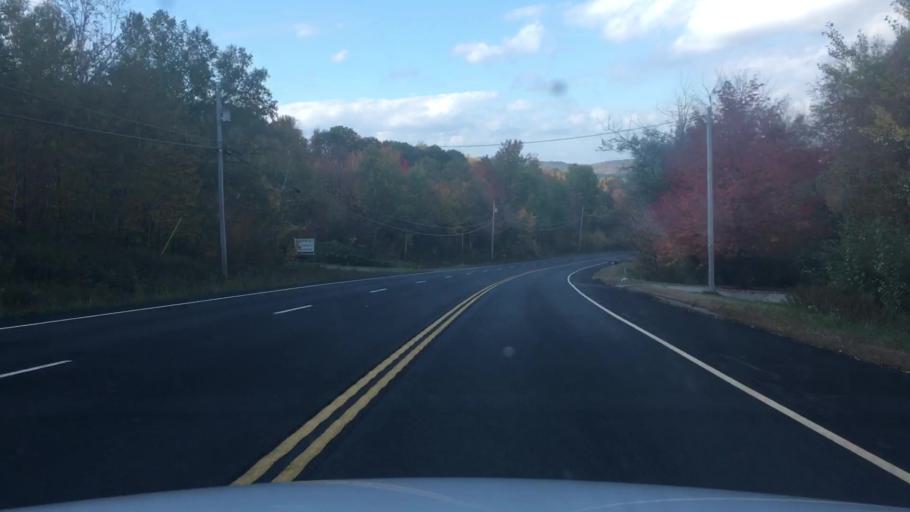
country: US
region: Maine
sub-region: Waldo County
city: Palermo
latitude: 44.3715
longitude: -69.3934
